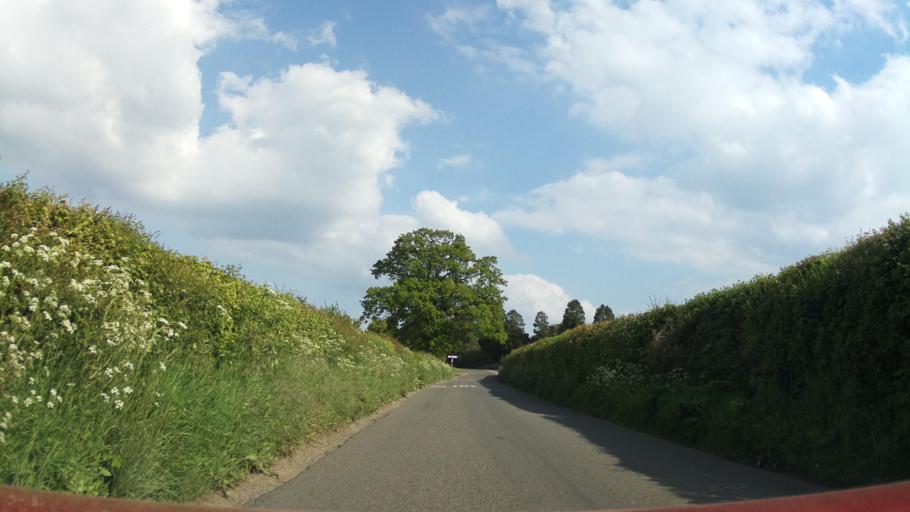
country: GB
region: England
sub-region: Wiltshire
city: Norton
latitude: 51.5424
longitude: -2.1484
